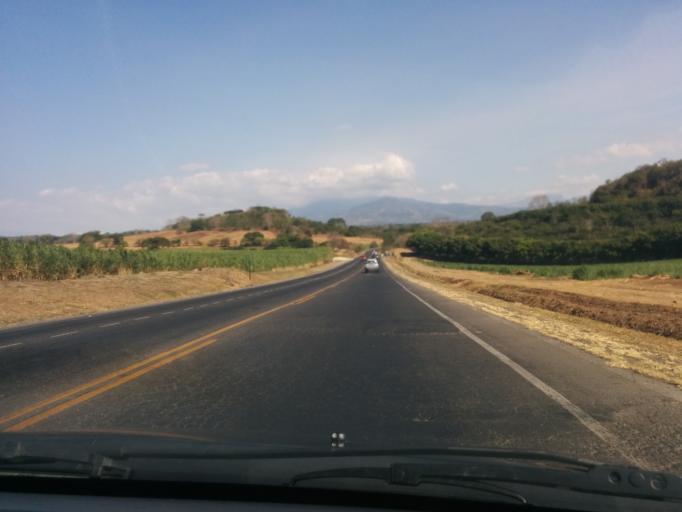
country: CR
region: Alajuela
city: Carrillos
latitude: 10.0084
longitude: -84.3231
